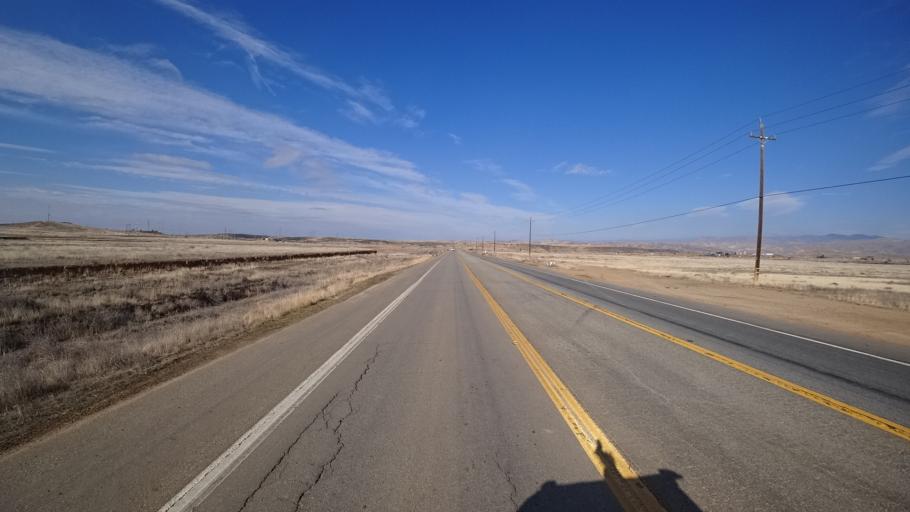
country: US
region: California
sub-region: Kern County
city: Oildale
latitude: 35.4094
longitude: -118.9142
